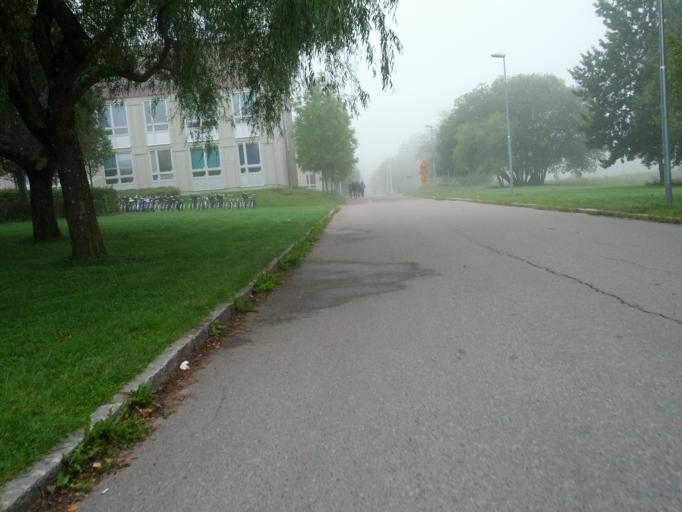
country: SE
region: Uppsala
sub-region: Uppsala Kommun
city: Uppsala
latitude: 59.8428
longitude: 17.6378
